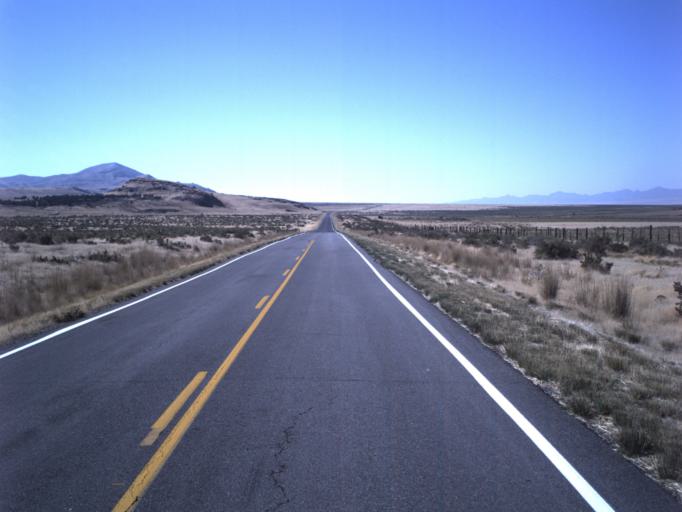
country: US
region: Utah
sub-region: Tooele County
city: Grantsville
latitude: 40.6250
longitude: -112.6983
